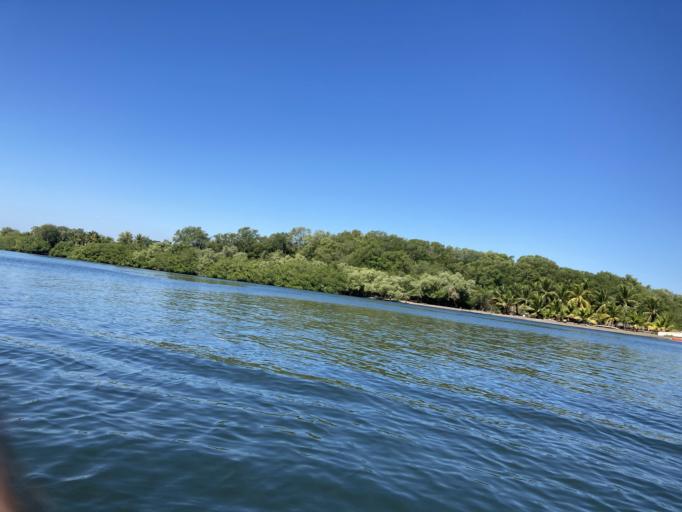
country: GT
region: Jutiapa
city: Pasaco
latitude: 13.8038
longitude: -90.2644
